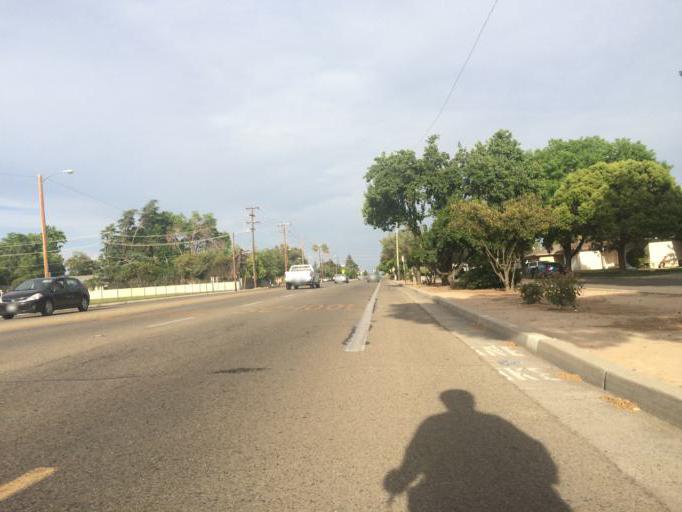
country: US
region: California
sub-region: Fresno County
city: Clovis
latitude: 36.8157
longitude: -119.7690
